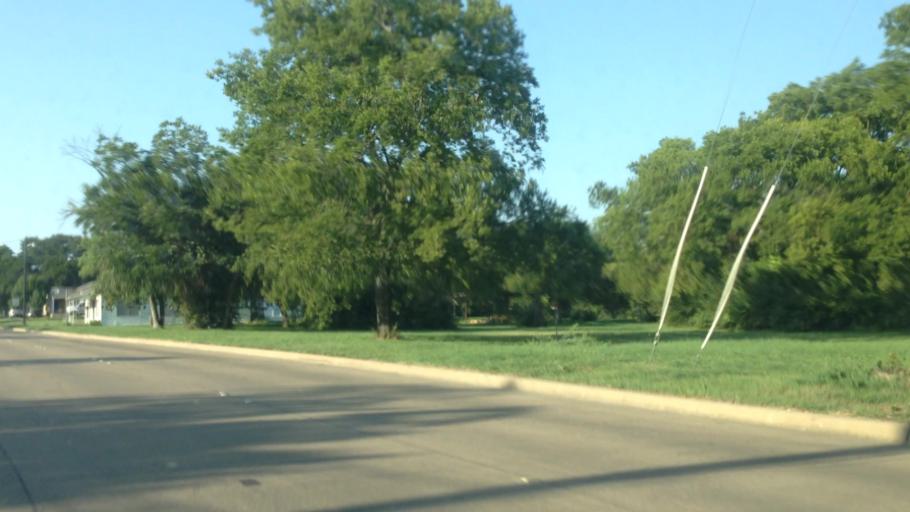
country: US
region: Texas
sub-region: Tarrant County
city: Haltom City
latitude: 32.8000
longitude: -97.2558
